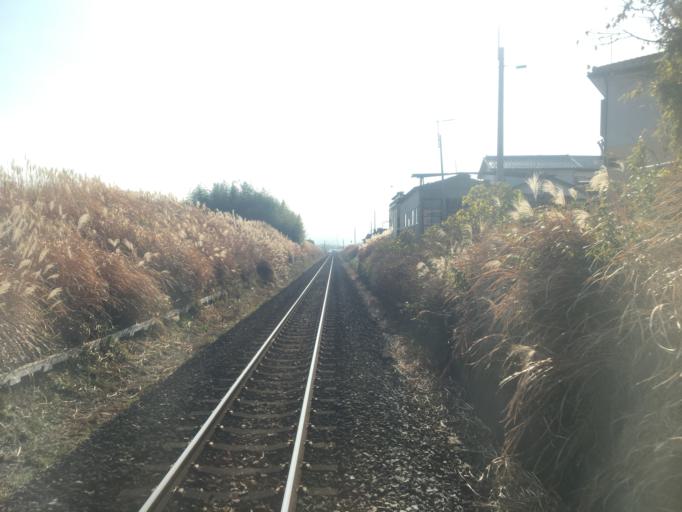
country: JP
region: Gunma
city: Fujioka
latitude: 36.2330
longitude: 139.0823
